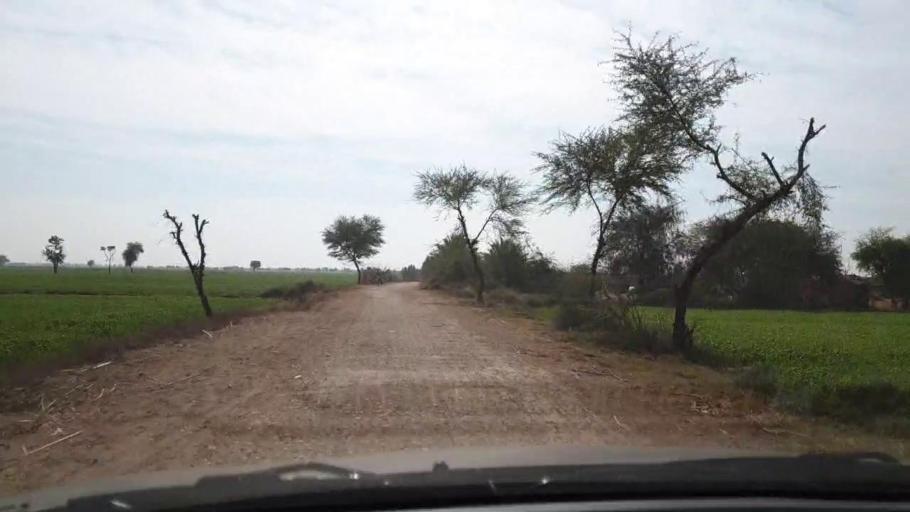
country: PK
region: Sindh
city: Jam Sahib
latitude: 26.2784
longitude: 68.6853
